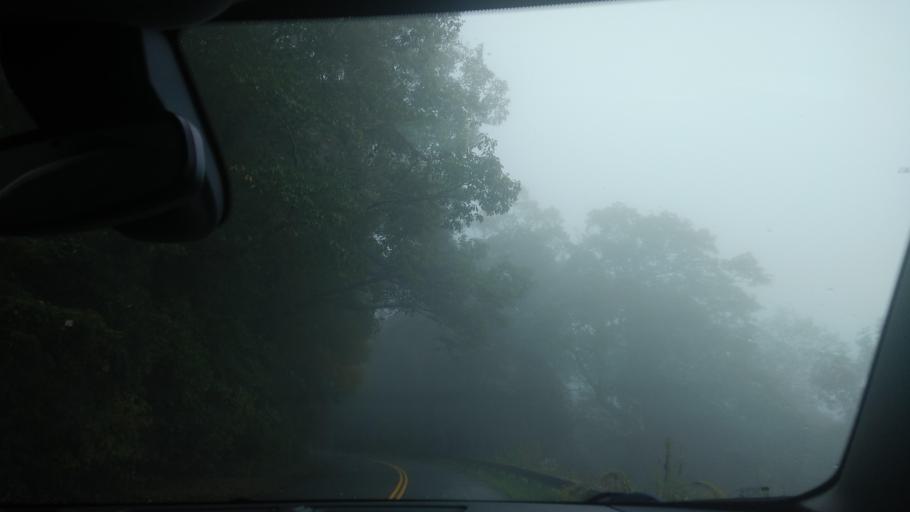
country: US
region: North Carolina
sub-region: Mitchell County
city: Spruce Pine
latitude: 35.9125
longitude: -81.9630
